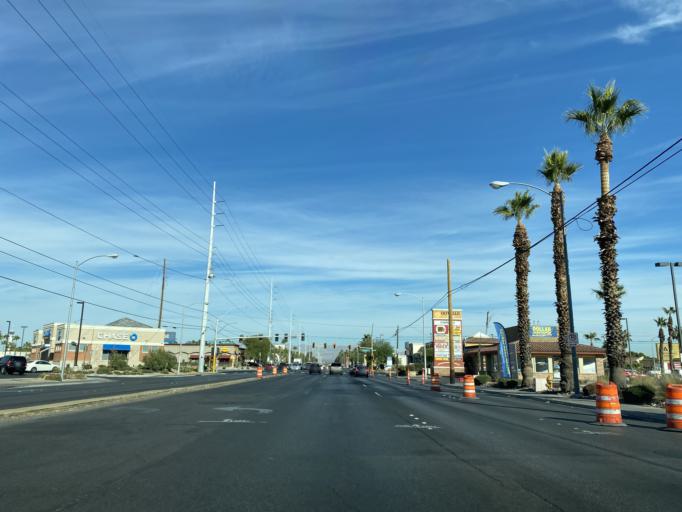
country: US
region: Nevada
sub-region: Clark County
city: Paradise
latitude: 36.0989
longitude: -115.1189
